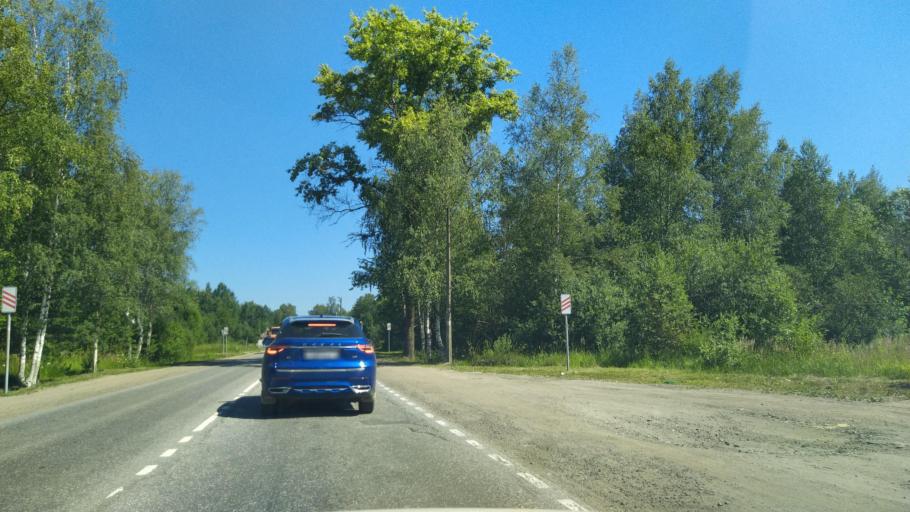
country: RU
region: Leningrad
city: Imeni Morozova
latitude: 59.9686
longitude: 31.0197
